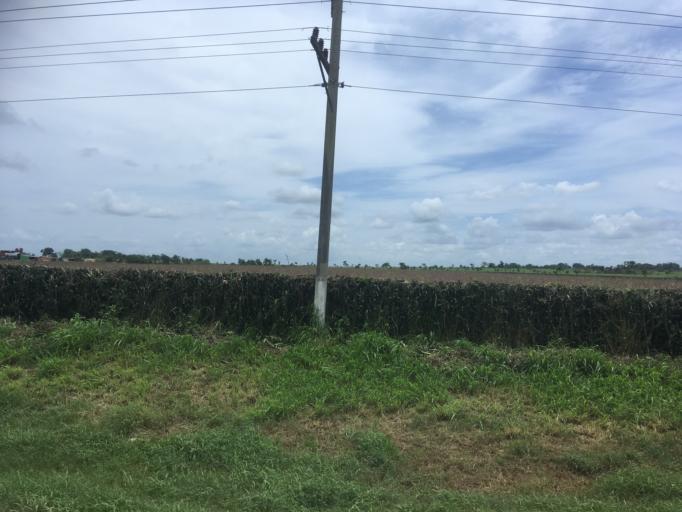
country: CU
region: Matanzas
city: Colon
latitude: 22.7032
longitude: -80.8749
